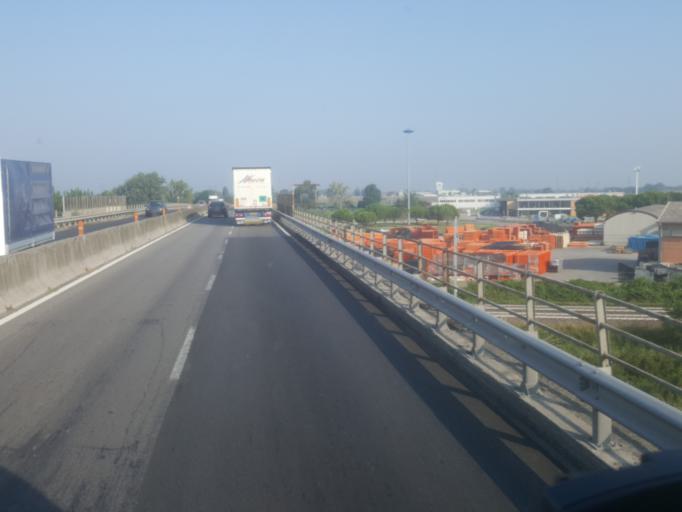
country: IT
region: Emilia-Romagna
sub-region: Provincia di Ravenna
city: Fornace Zarattini
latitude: 44.4210
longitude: 12.1642
